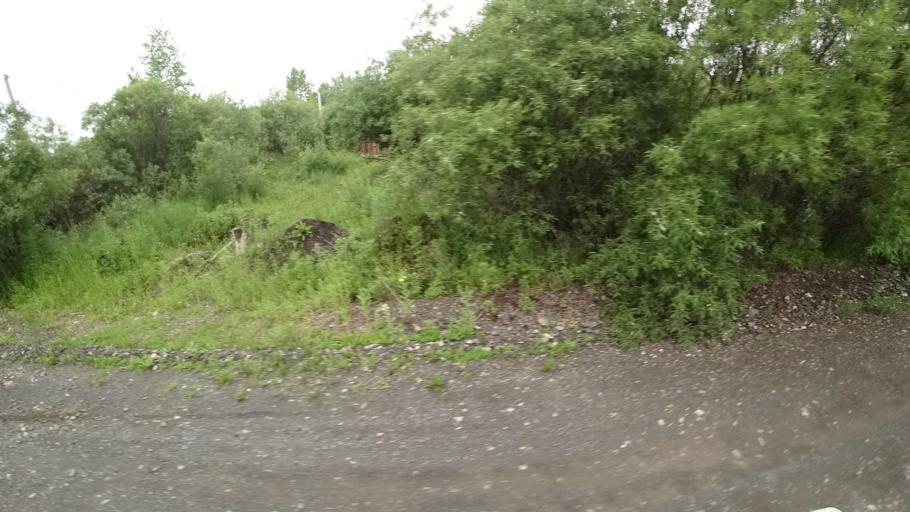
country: RU
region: Khabarovsk Krai
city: Amursk
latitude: 49.9089
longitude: 136.1496
